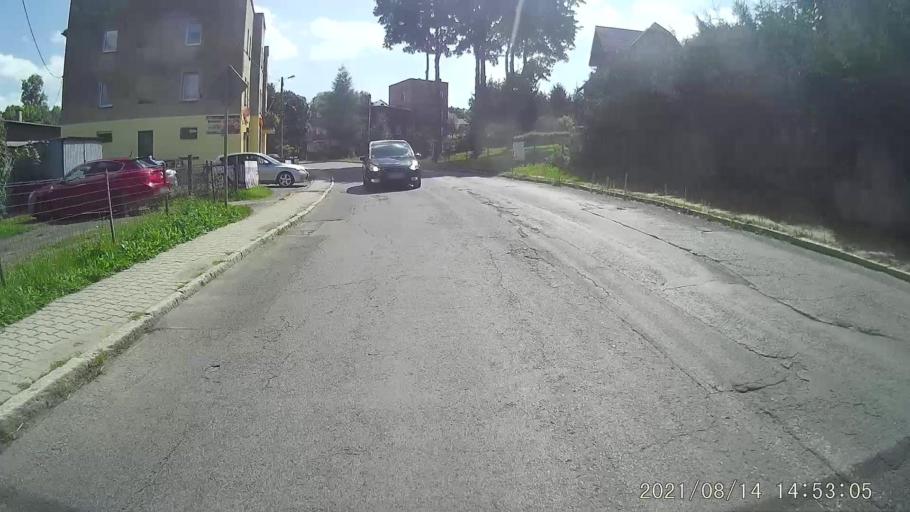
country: PL
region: Lower Silesian Voivodeship
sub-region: Powiat walbrzyski
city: Gluszyca Gorna
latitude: 50.6719
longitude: 16.3751
